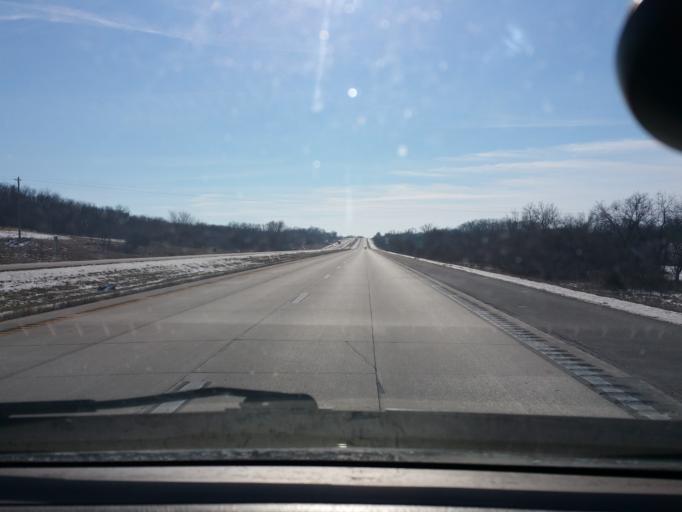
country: US
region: Missouri
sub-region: Daviess County
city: Gallatin
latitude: 39.9898
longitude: -94.0954
